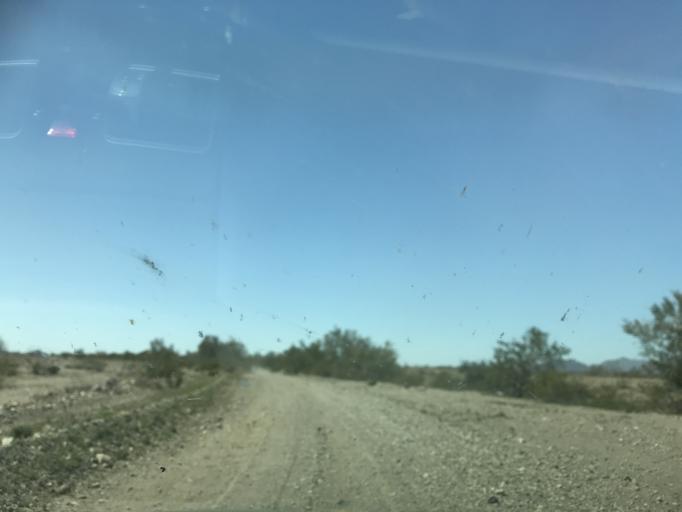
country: US
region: California
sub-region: Riverside County
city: Mesa Verde
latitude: 33.4762
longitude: -114.9445
